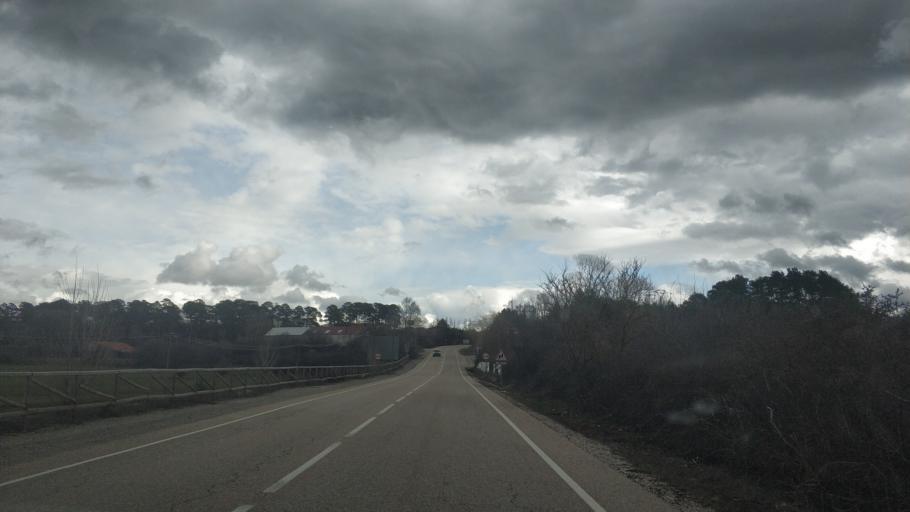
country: ES
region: Castille and Leon
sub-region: Provincia de Burgos
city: Quintanar de la Sierra
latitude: 41.9736
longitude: -3.0433
